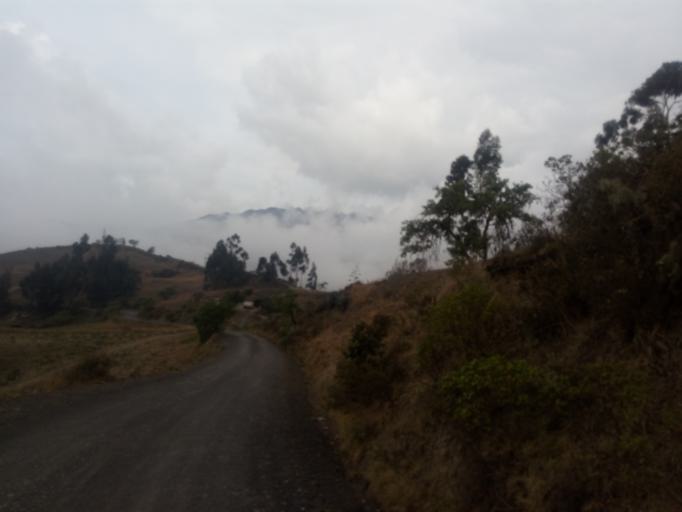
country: CO
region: Boyaca
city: Chita
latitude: 6.1917
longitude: -72.4906
